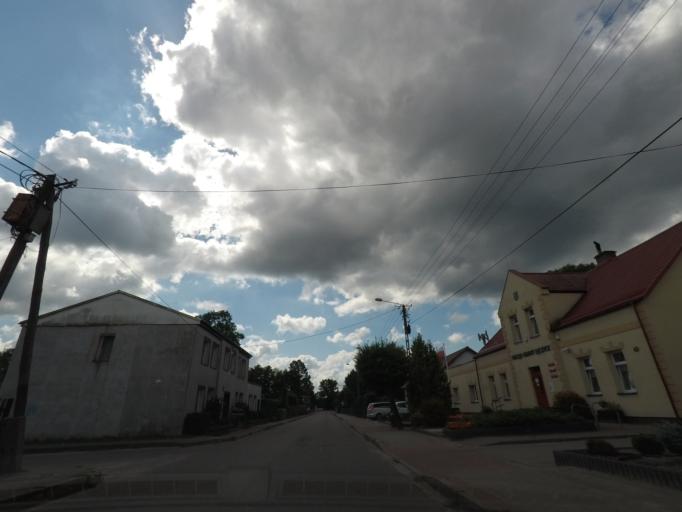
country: PL
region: Pomeranian Voivodeship
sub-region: Powiat wejherowski
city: Leczyce
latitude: 54.5918
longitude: 17.8614
